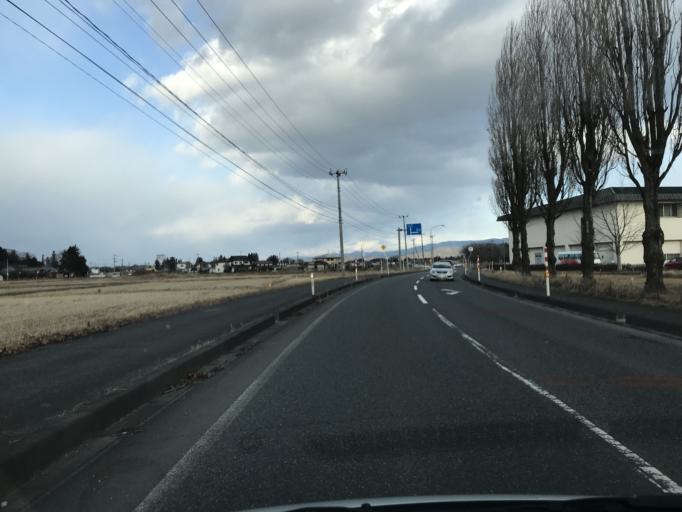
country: JP
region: Iwate
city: Mizusawa
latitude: 39.0582
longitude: 141.1402
